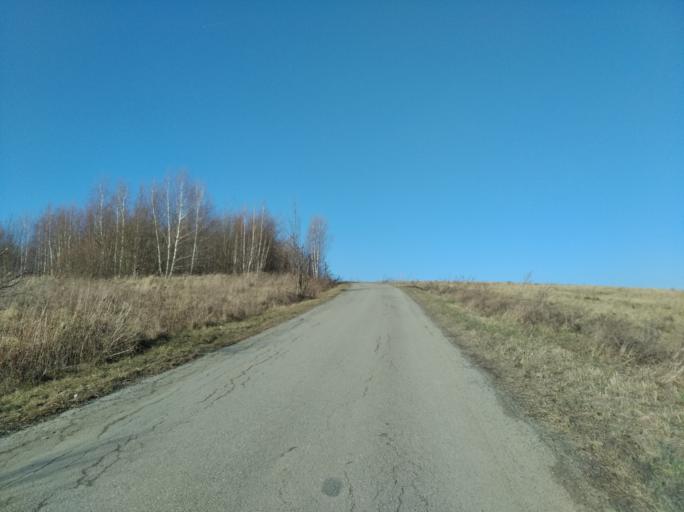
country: PL
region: Subcarpathian Voivodeship
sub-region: Powiat strzyzowski
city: Jawornik
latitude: 49.8283
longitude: 21.8708
